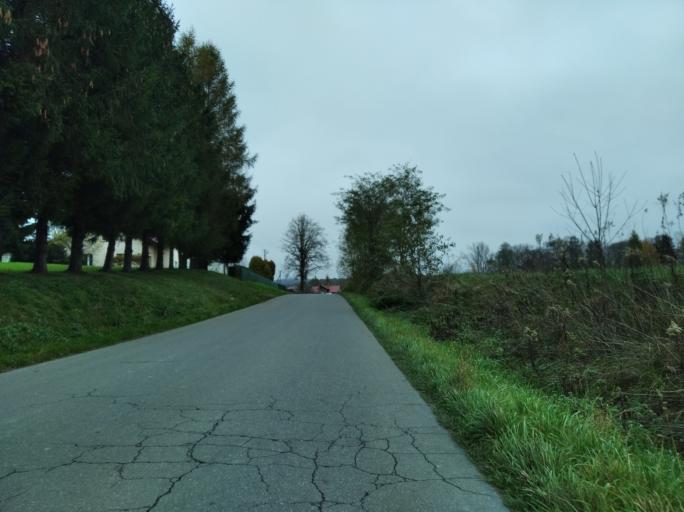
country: PL
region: Subcarpathian Voivodeship
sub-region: Powiat krosnienski
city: Leki
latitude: 49.8008
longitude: 21.6697
